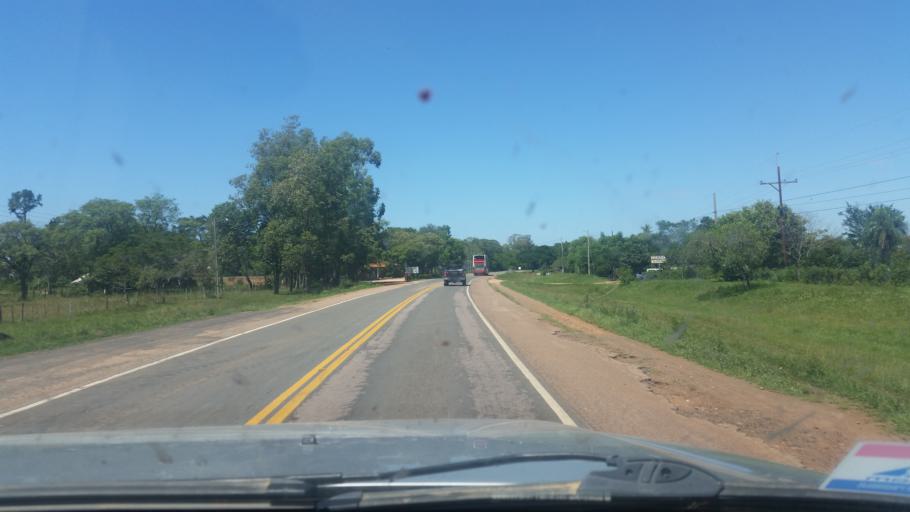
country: PY
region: Paraguari
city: Caapucu
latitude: -26.2401
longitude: -57.1745
